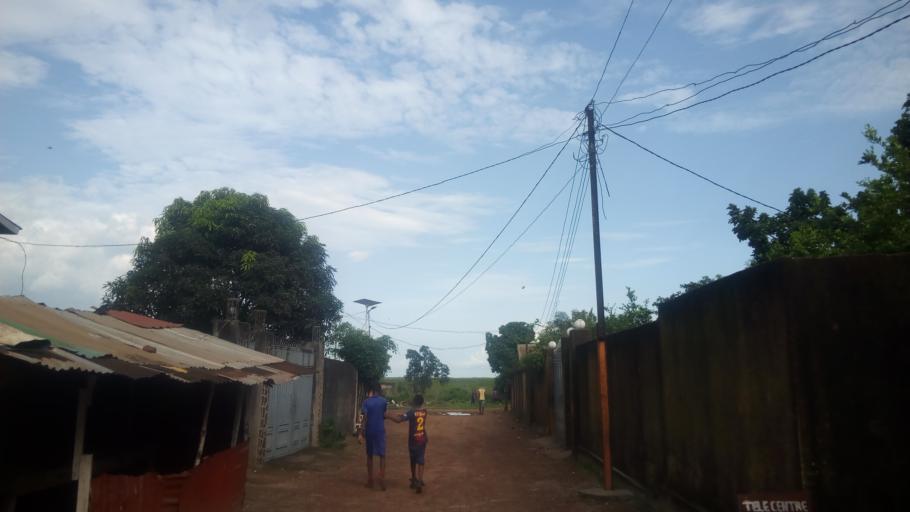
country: GN
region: Kindia
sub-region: Prefecture de Dubreka
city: Dubreka
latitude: 9.6485
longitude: -13.5330
